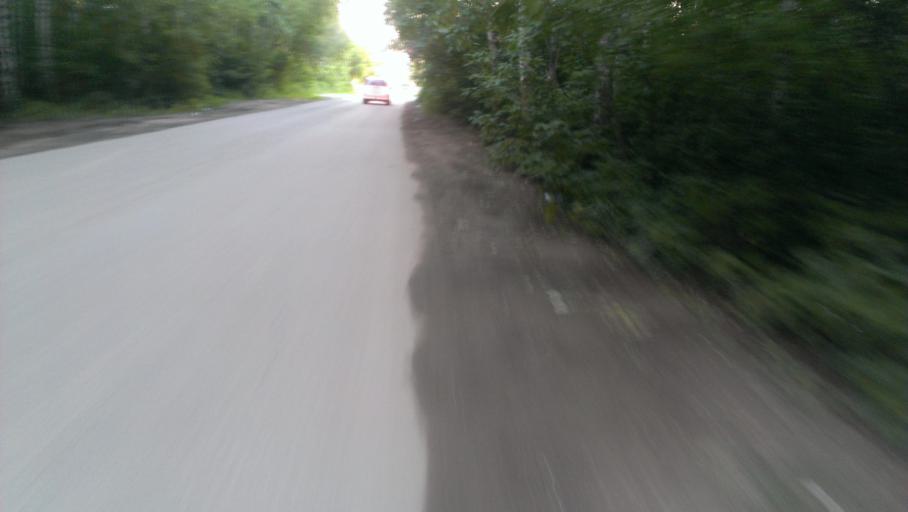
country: RU
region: Altai Krai
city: Novosilikatnyy
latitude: 53.3635
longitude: 83.6579
